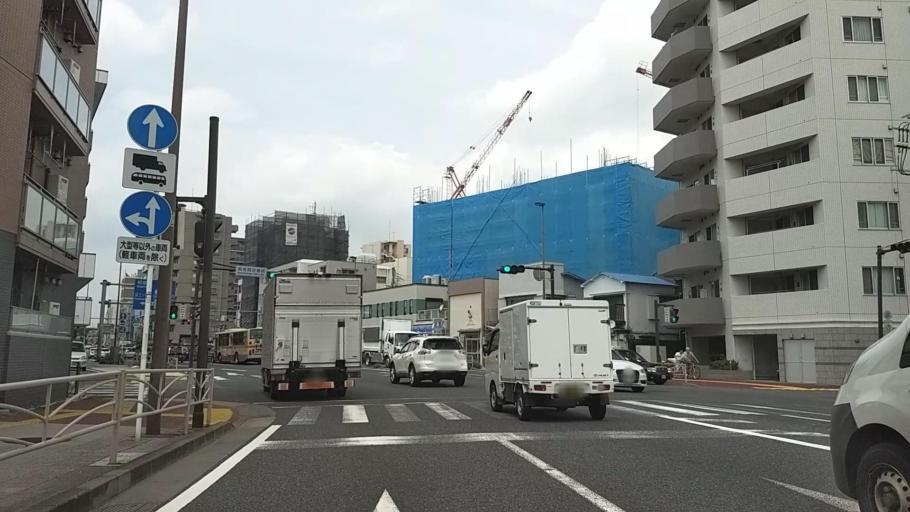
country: JP
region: Kanagawa
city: Yokohama
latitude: 35.4560
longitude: 139.6078
